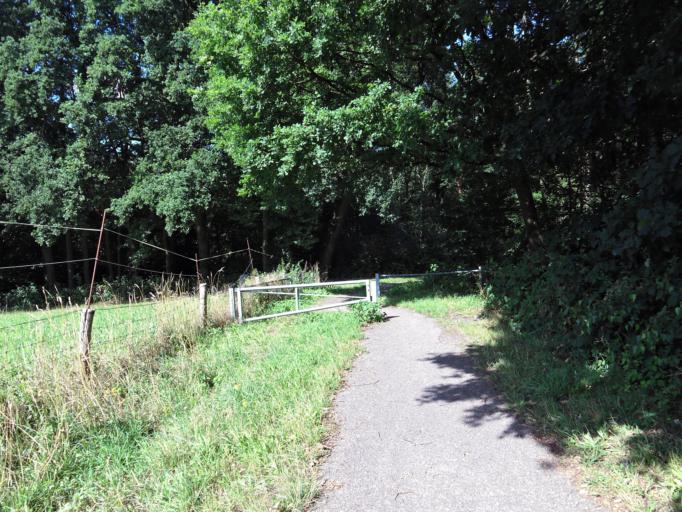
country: NL
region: Limburg
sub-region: Gemeente Onderbanken
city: Schinveld
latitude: 50.9538
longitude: 5.9868
